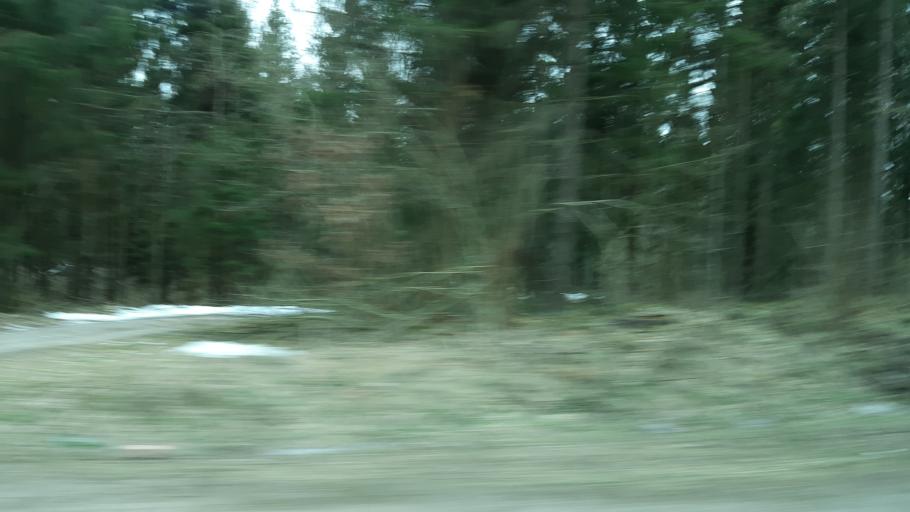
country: PL
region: Podlasie
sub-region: Suwalki
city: Suwalki
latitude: 54.2993
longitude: 22.9568
